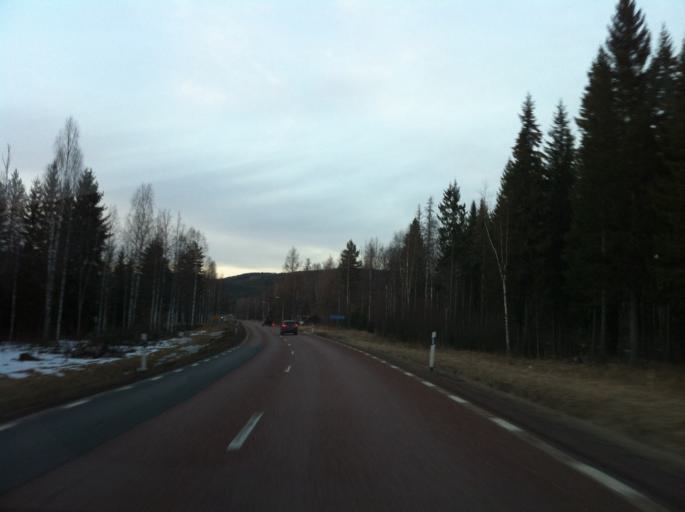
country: SE
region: Dalarna
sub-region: Mora Kommun
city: Mora
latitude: 60.8805
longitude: 14.3735
